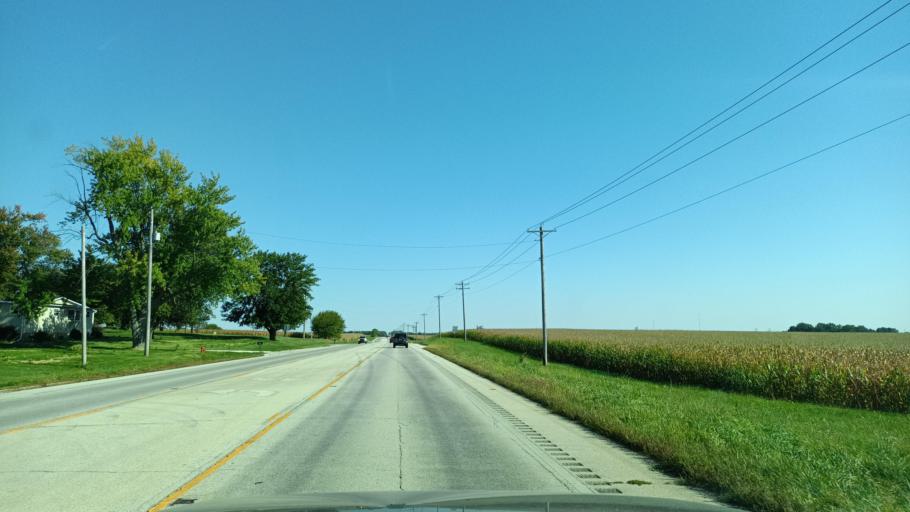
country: US
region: Illinois
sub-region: Champaign County
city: Lake of the Woods
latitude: 40.1804
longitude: -88.3565
